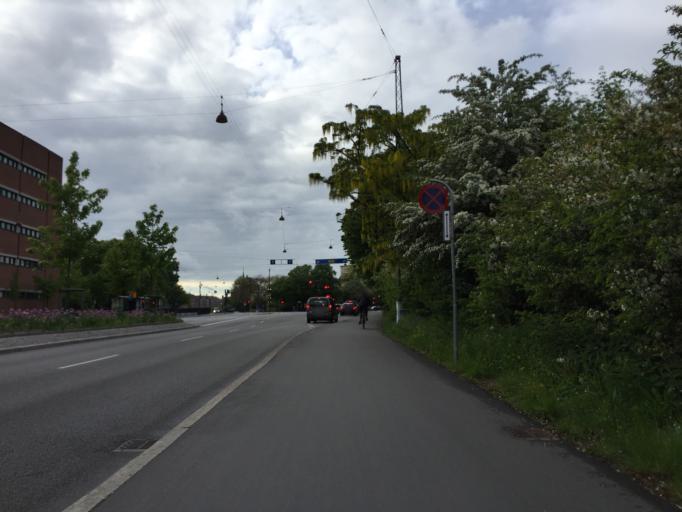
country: DK
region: Capital Region
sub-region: Kobenhavn
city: Copenhagen
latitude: 55.6955
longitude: 12.5633
